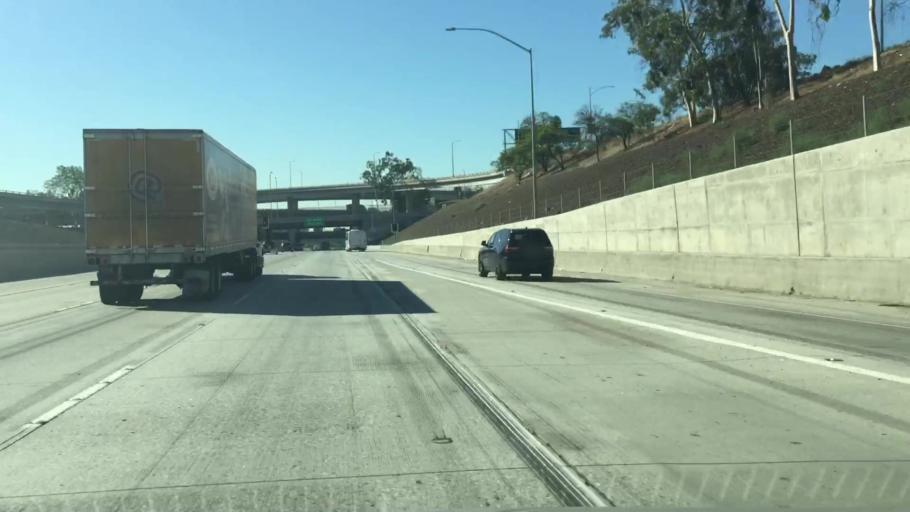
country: US
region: California
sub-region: Los Angeles County
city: Belvedere
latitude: 34.0388
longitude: -118.1702
